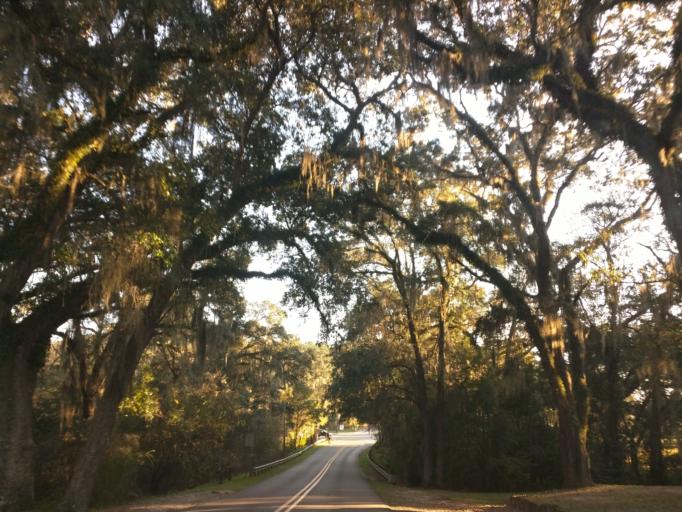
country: US
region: Florida
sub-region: Leon County
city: Tallahassee
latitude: 30.4415
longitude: -84.2188
